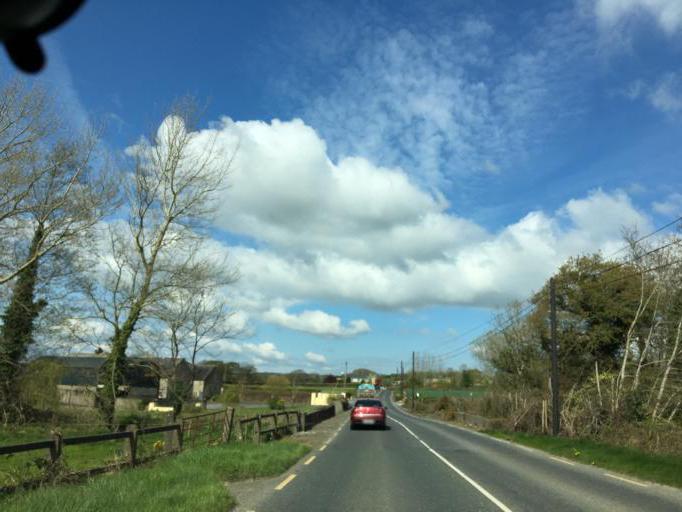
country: IE
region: Leinster
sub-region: Loch Garman
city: New Ross
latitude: 52.4333
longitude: -6.9559
